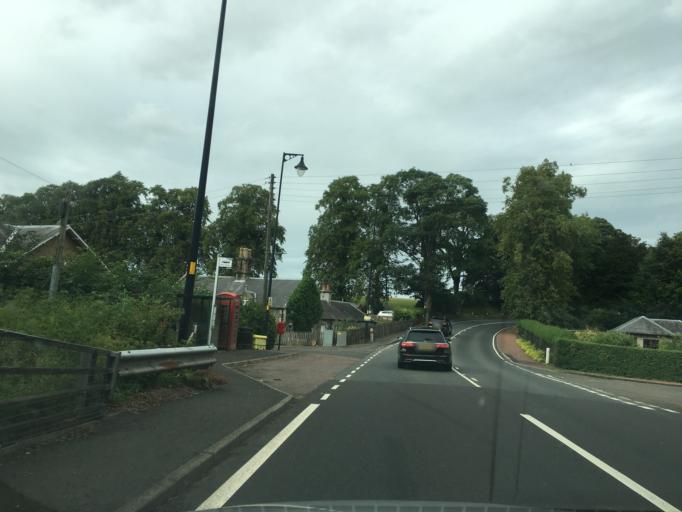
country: GB
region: Scotland
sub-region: South Lanarkshire
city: Biggar
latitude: 55.5624
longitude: -3.6188
